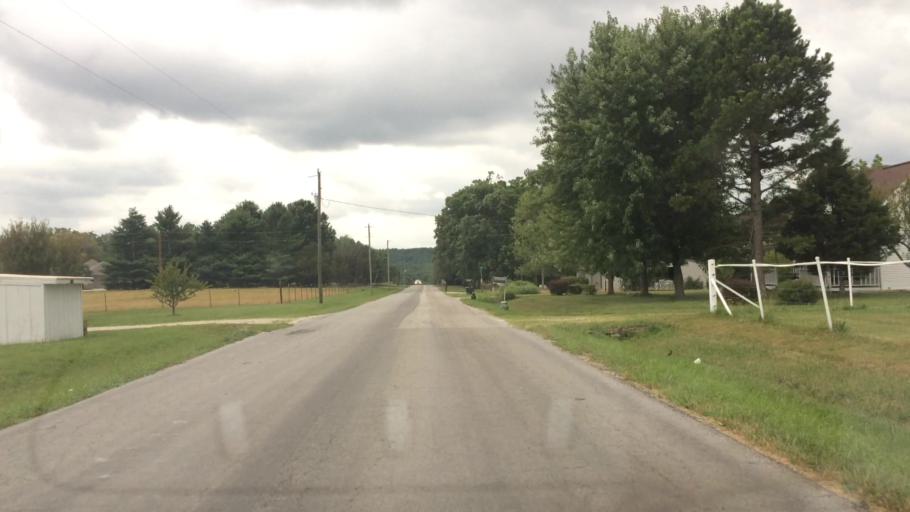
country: US
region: Missouri
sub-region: Webster County
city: Marshfield
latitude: 37.3107
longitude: -92.9845
